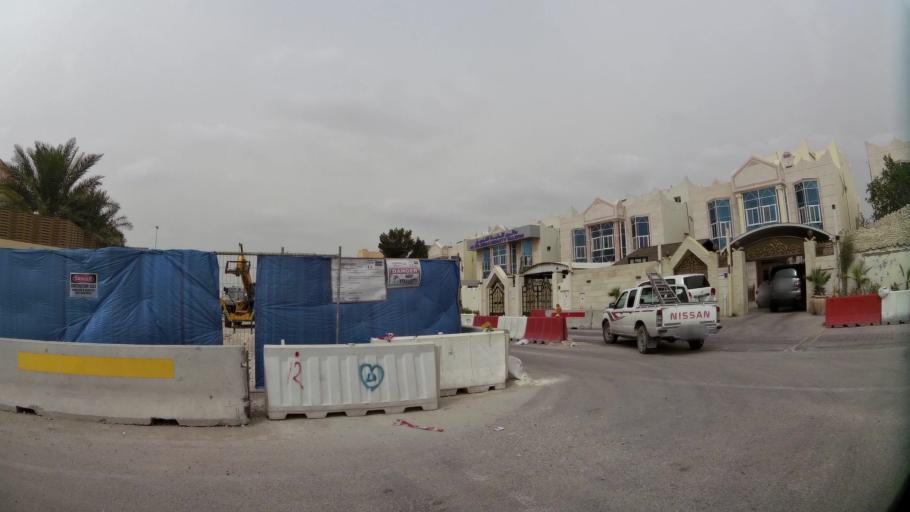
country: QA
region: Baladiyat ad Dawhah
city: Doha
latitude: 25.2524
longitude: 51.5152
